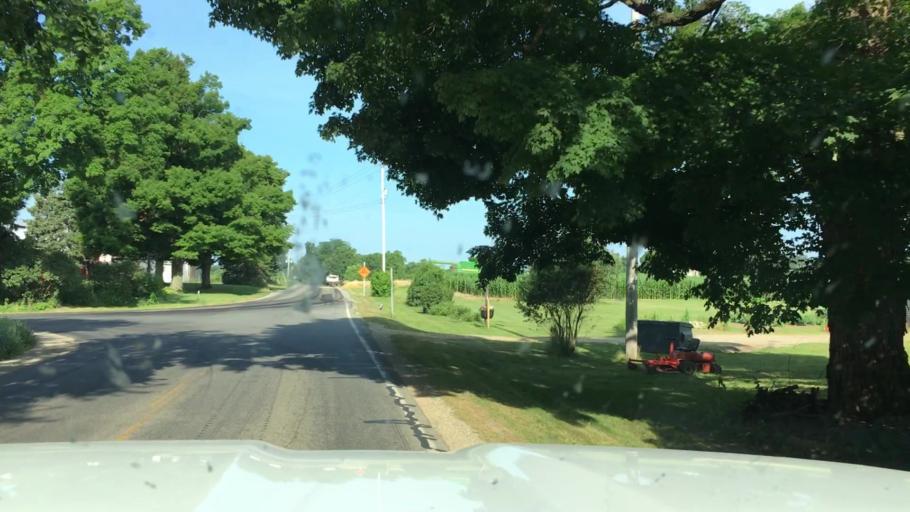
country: US
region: Michigan
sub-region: Barry County
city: Stony Point
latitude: 42.4570
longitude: -85.4546
